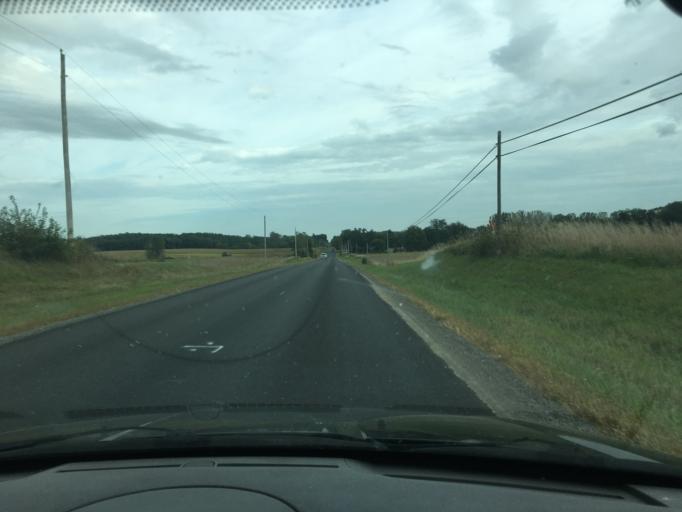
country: US
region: Ohio
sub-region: Logan County
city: Bellefontaine
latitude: 40.3253
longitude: -83.7341
